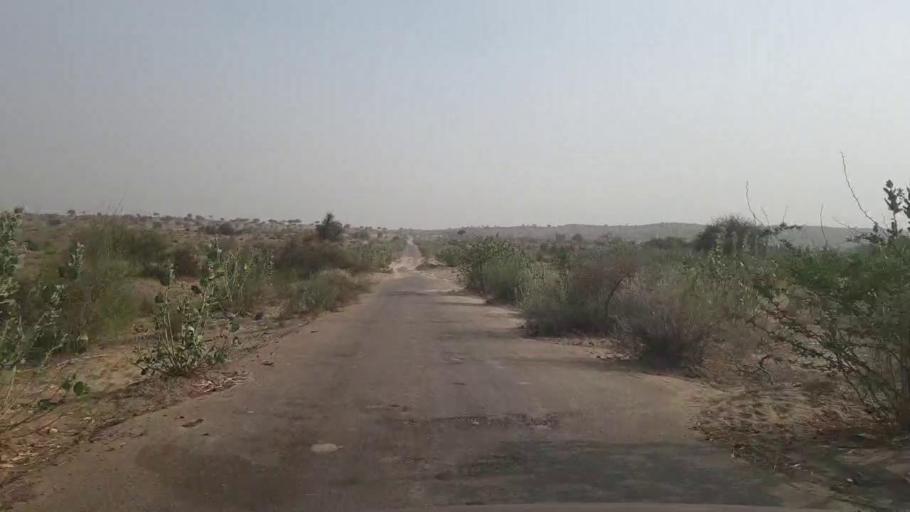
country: PK
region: Sindh
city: Chor
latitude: 25.5200
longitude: 69.9636
